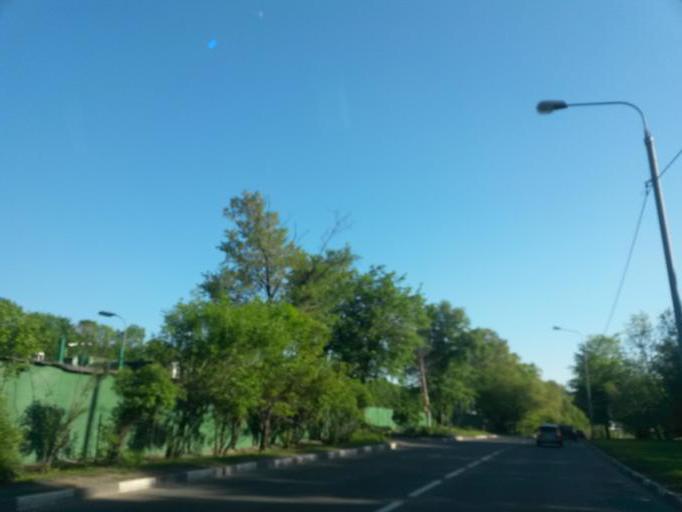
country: RU
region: Moscow
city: Orekhovo-Borisovo Severnoye
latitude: 55.6318
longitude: 37.6844
